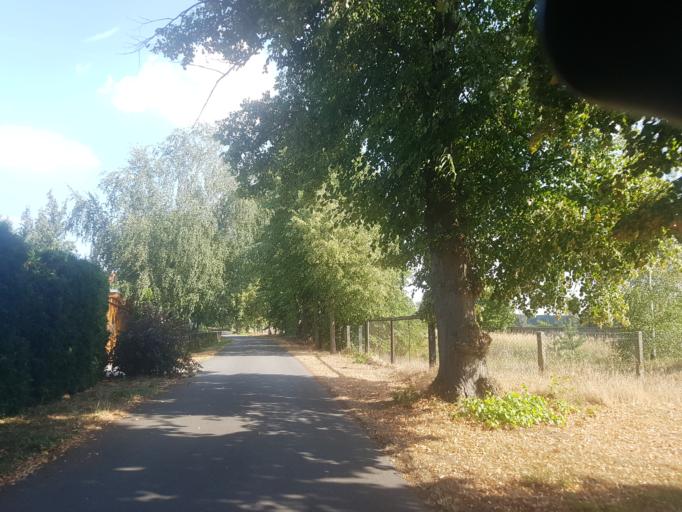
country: DE
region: Saxony-Anhalt
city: Holzdorf
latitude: 51.8134
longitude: 13.2249
